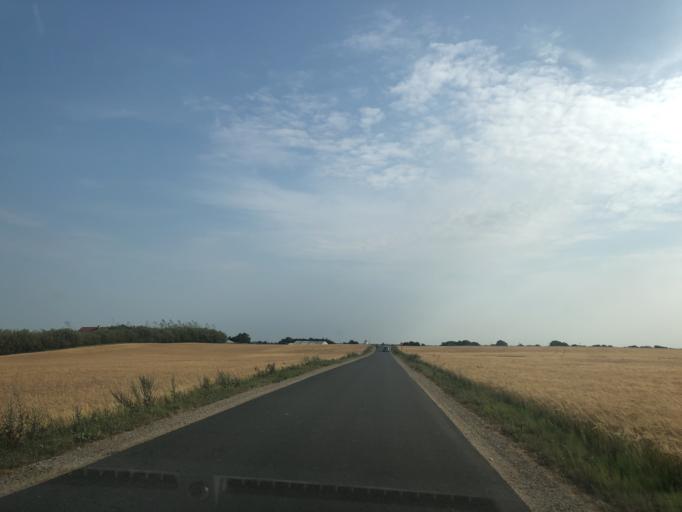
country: DK
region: North Denmark
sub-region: Morso Kommune
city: Nykobing Mors
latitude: 56.8246
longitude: 9.0191
